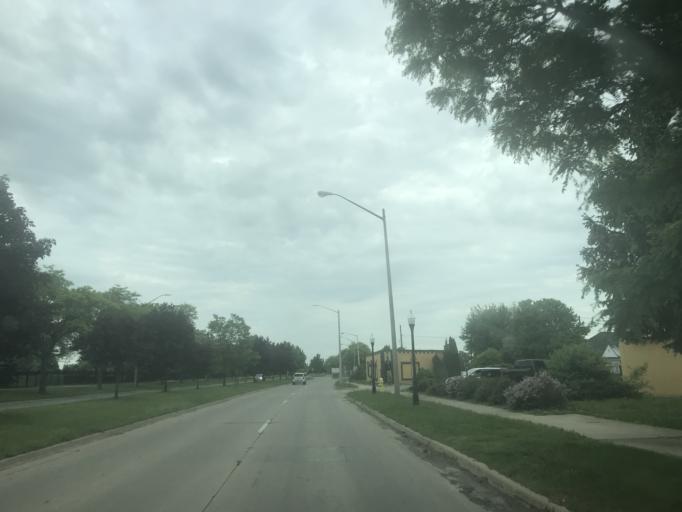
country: US
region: Michigan
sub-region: Wayne County
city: Wyandotte
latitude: 42.1942
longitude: -83.1537
